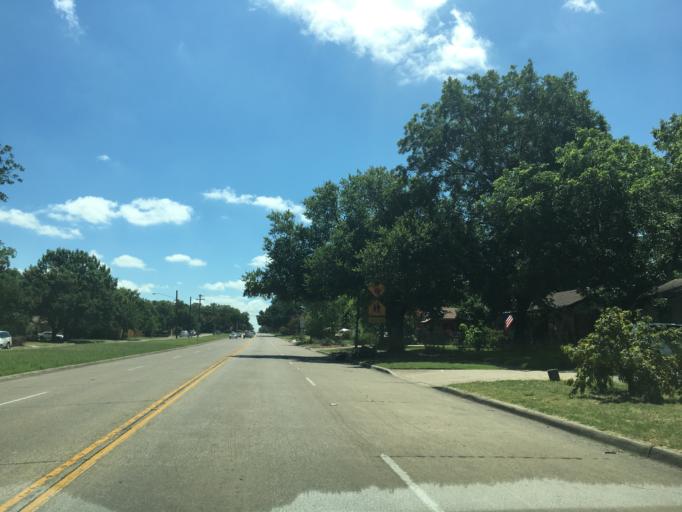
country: US
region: Texas
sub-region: Dallas County
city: Garland
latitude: 32.8429
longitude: -96.6750
